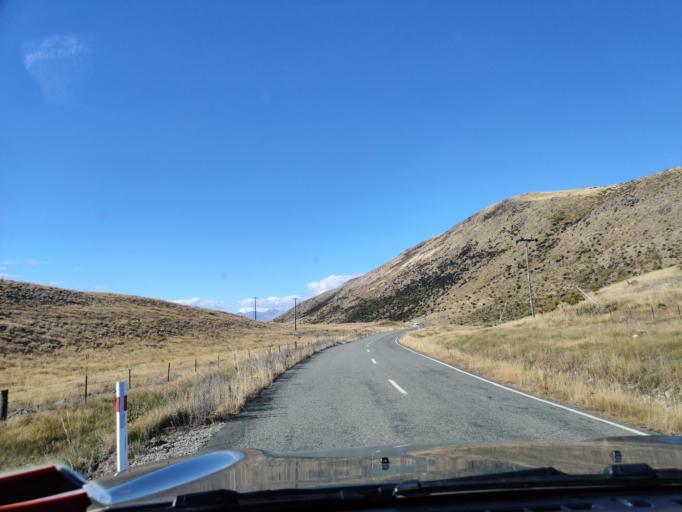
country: NZ
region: Canterbury
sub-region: Timaru District
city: Pleasant Point
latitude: -43.9895
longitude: 170.4510
